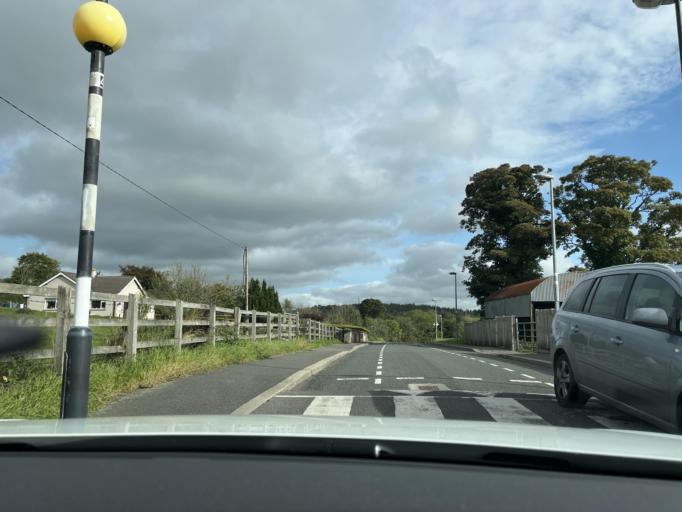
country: IE
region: Connaught
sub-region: County Leitrim
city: Carrick-on-Shannon
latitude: 53.9551
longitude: -8.0671
